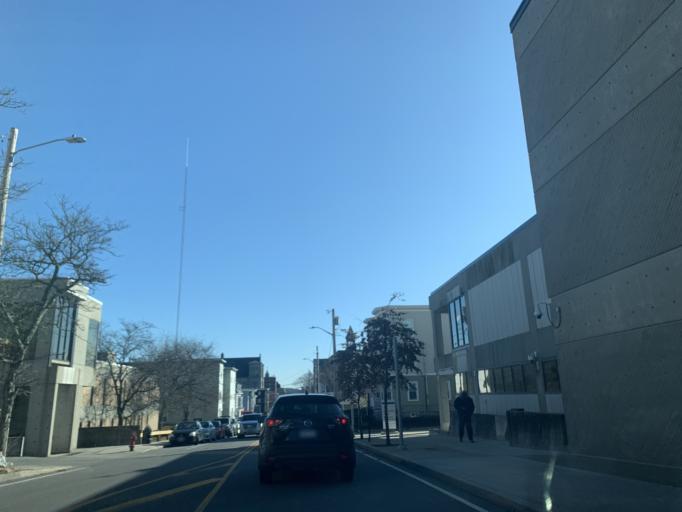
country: US
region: Massachusetts
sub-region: Middlesex County
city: Lowell
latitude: 42.6504
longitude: -71.3234
